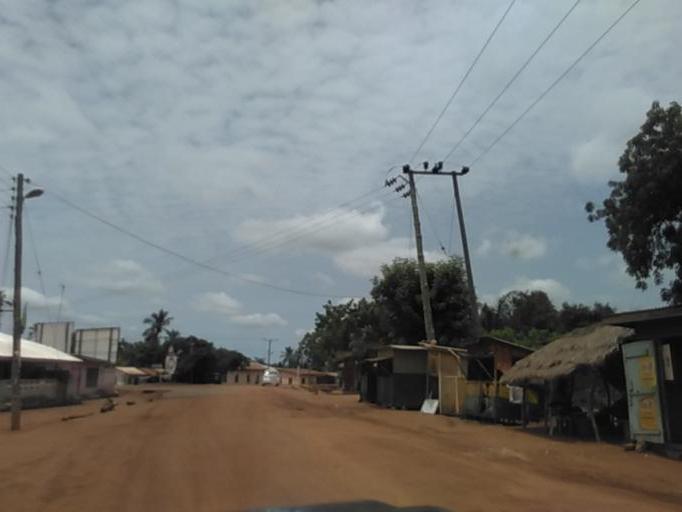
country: GH
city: Akropong
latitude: 6.0298
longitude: 0.3757
